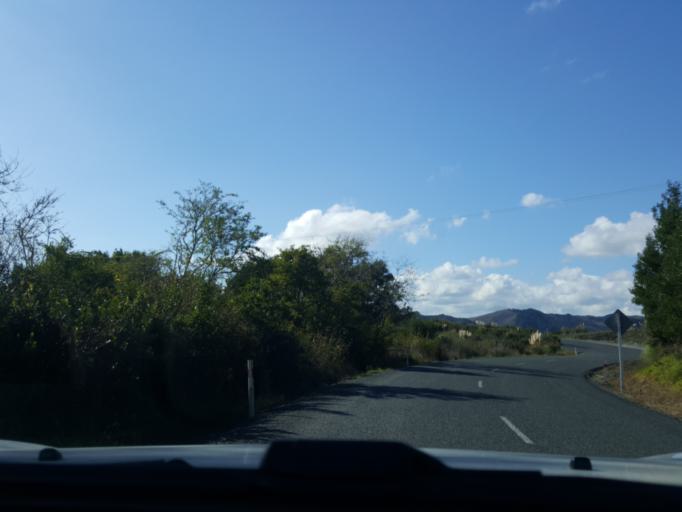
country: NZ
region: Waikato
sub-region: Waikato District
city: Ngaruawahia
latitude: -37.5396
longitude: 175.1742
